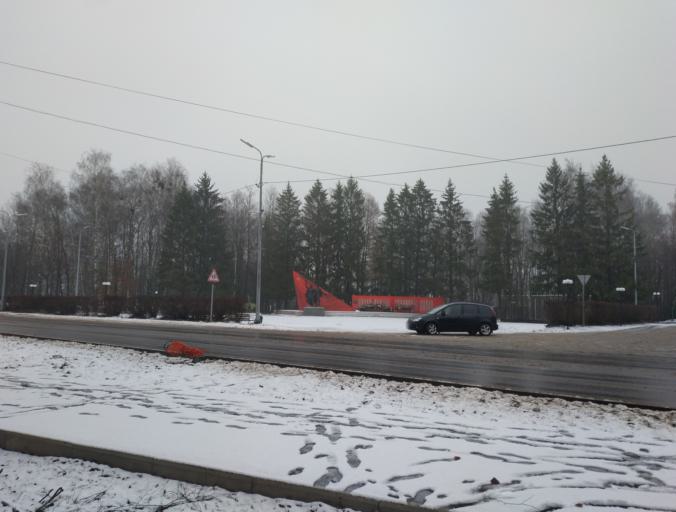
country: RU
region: Moskovskaya
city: Taldom
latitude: 56.7397
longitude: 37.5371
